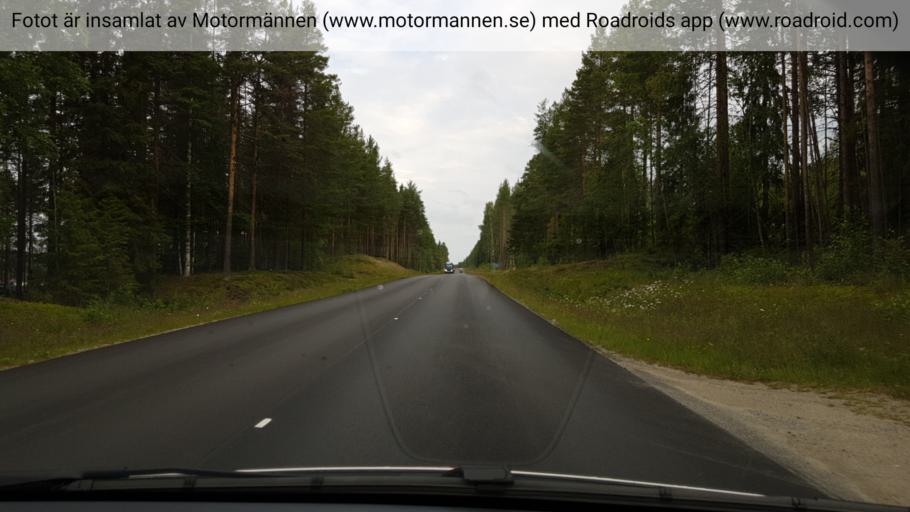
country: SE
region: Vaesterbotten
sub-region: Lycksele Kommun
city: Lycksele
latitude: 64.5510
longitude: 18.7358
